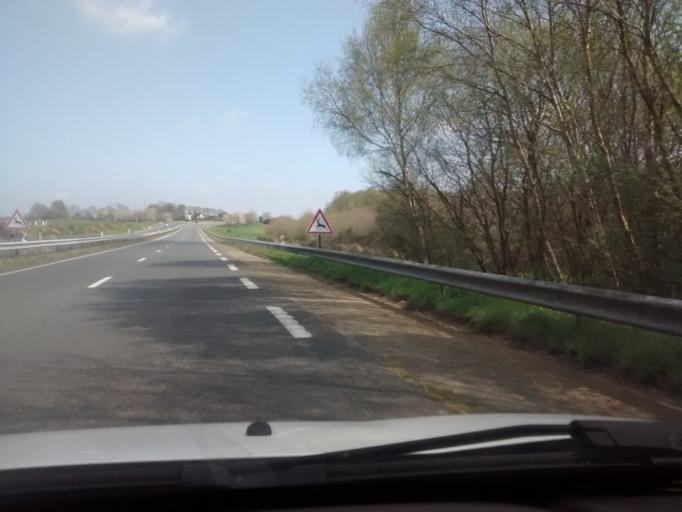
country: FR
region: Brittany
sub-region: Departement des Cotes-d'Armor
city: Plouisy
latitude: 48.5739
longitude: -3.2189
